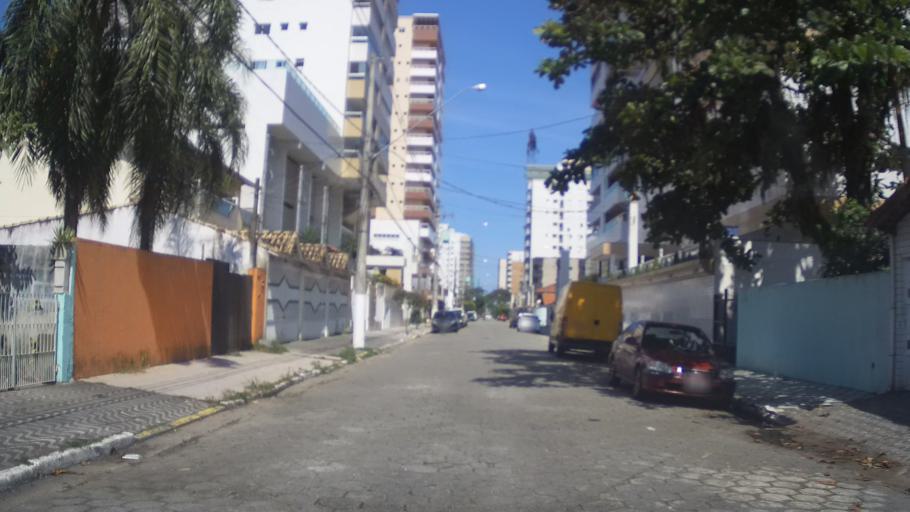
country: BR
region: Sao Paulo
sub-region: Praia Grande
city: Praia Grande
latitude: -24.0088
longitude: -46.4278
